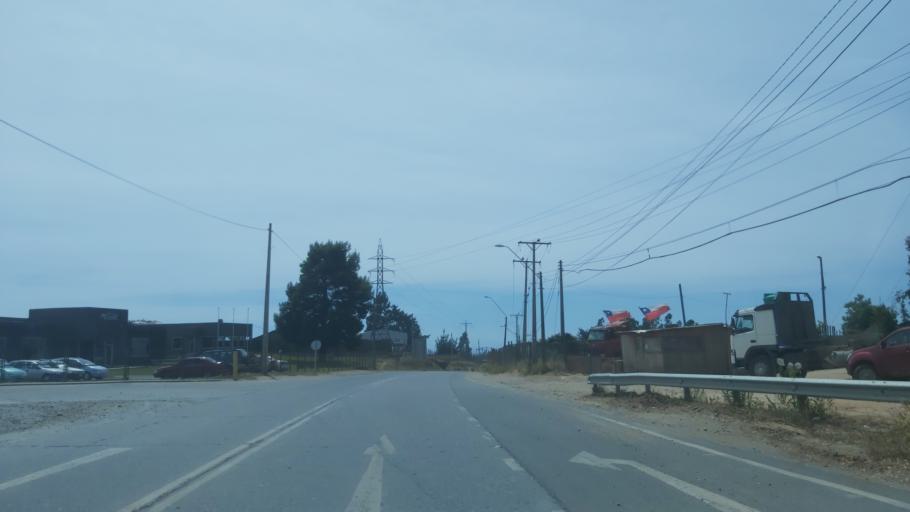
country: CL
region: Maule
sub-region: Provincia de Talca
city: Constitucion
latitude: -35.3631
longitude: -72.4040
